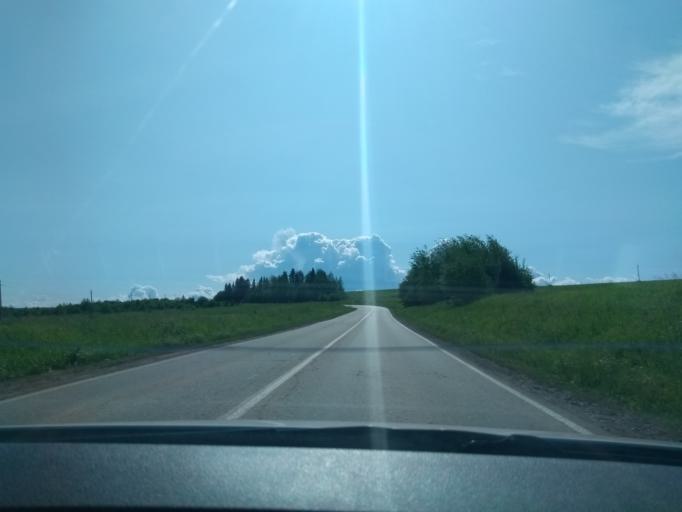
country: RU
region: Perm
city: Lobanovo
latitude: 57.8539
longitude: 56.3240
